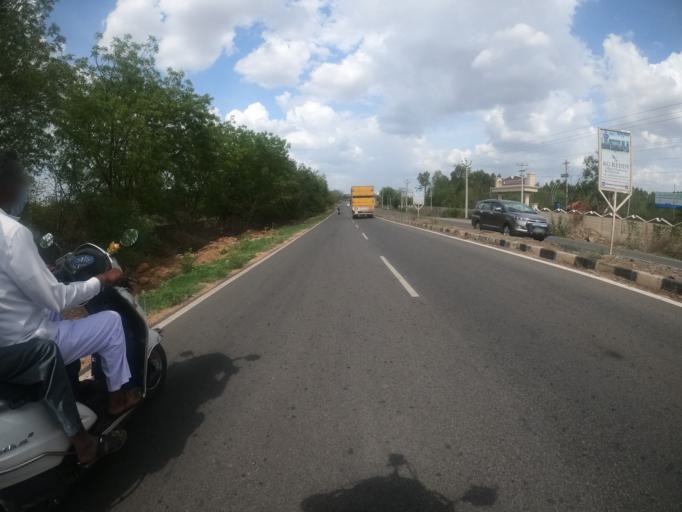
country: IN
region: Telangana
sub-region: Rangareddi
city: Sriramnagar
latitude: 17.3312
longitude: 78.2929
